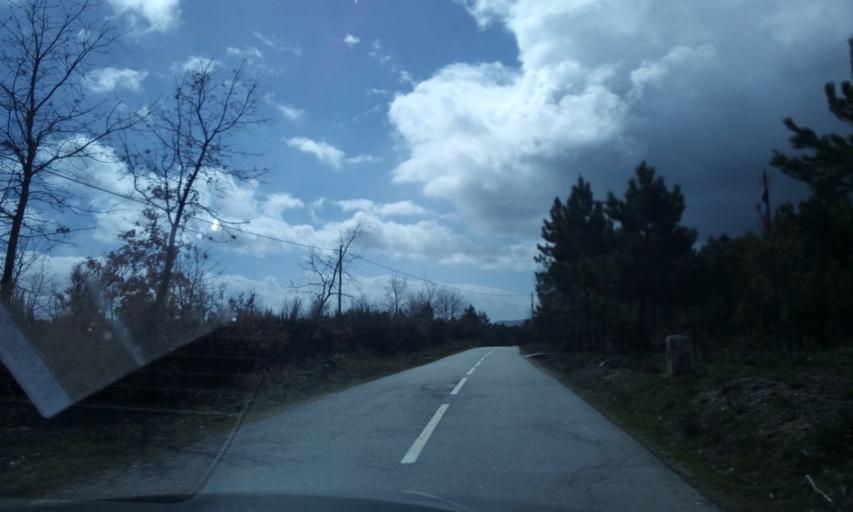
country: PT
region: Guarda
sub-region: Fornos de Algodres
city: Fornos de Algodres
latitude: 40.6384
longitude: -7.5517
